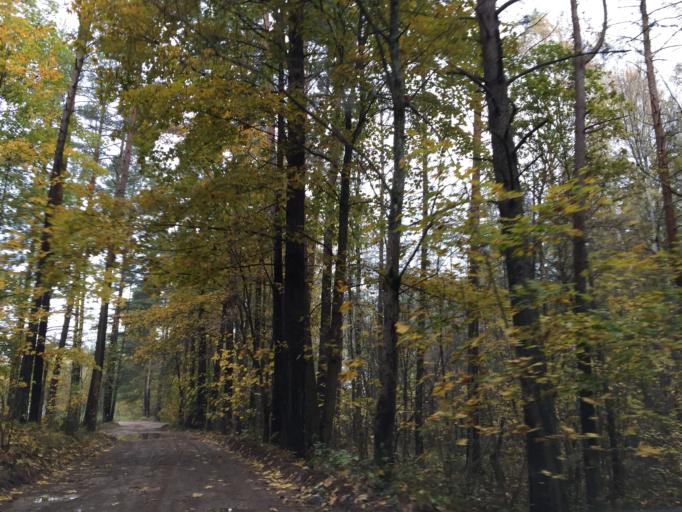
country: LV
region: Ogre
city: Ogre
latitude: 56.7998
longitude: 24.6469
